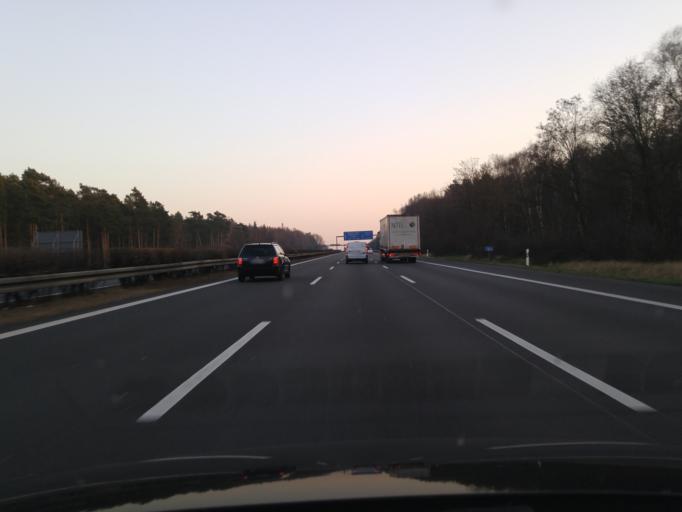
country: DE
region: Brandenburg
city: Fichtenwalde
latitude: 52.3011
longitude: 12.8946
